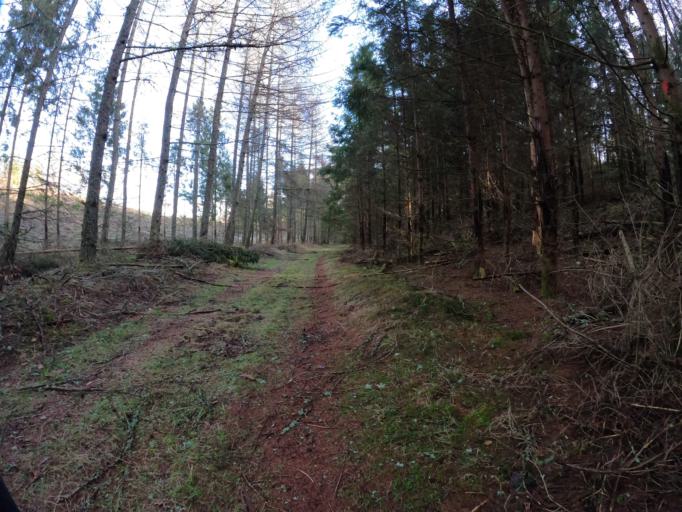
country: PL
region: West Pomeranian Voivodeship
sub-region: Powiat koszalinski
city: Polanow
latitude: 54.1916
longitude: 16.6680
